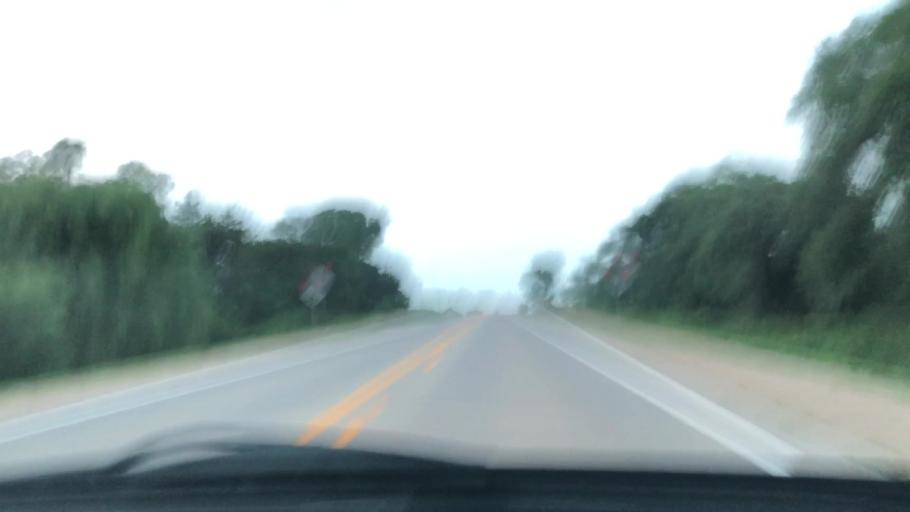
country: US
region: Iowa
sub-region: Linn County
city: Ely
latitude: 41.8500
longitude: -91.6754
